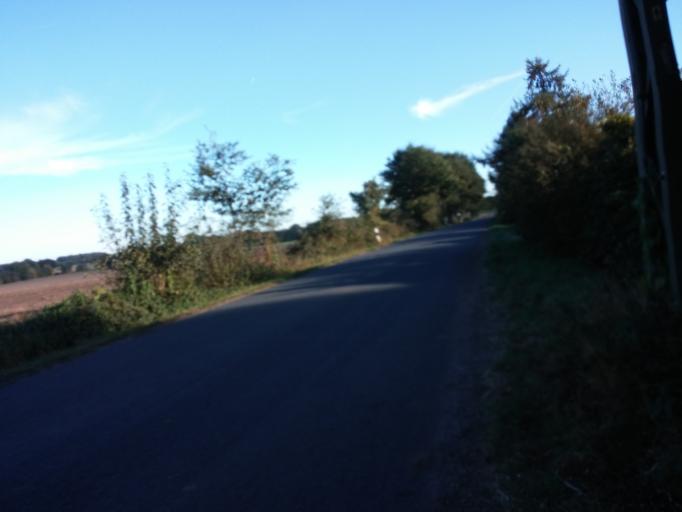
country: DE
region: North Rhine-Westphalia
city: Dorsten
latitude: 51.6456
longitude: 6.9959
